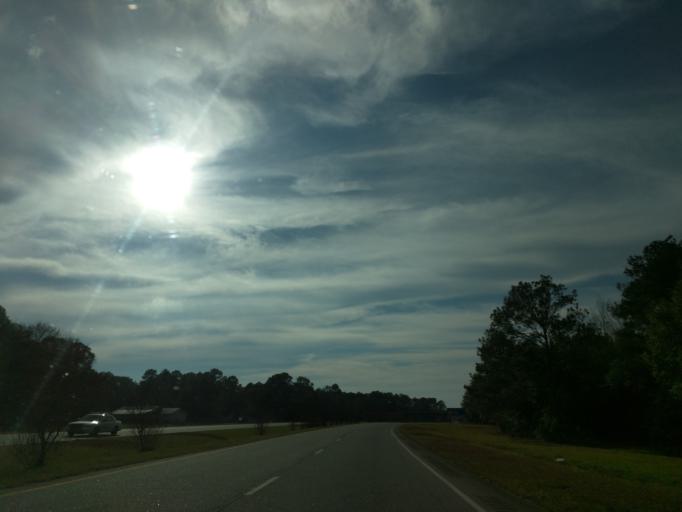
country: US
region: Georgia
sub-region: Decatur County
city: Bainbridge
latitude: 30.8914
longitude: -84.5578
